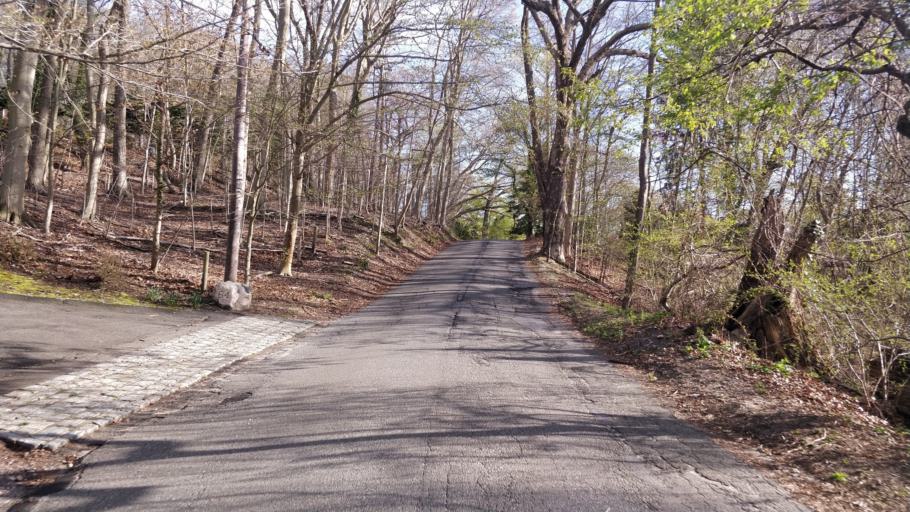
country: US
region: New York
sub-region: Suffolk County
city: Head of the Harbor
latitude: 40.8986
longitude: -73.1676
